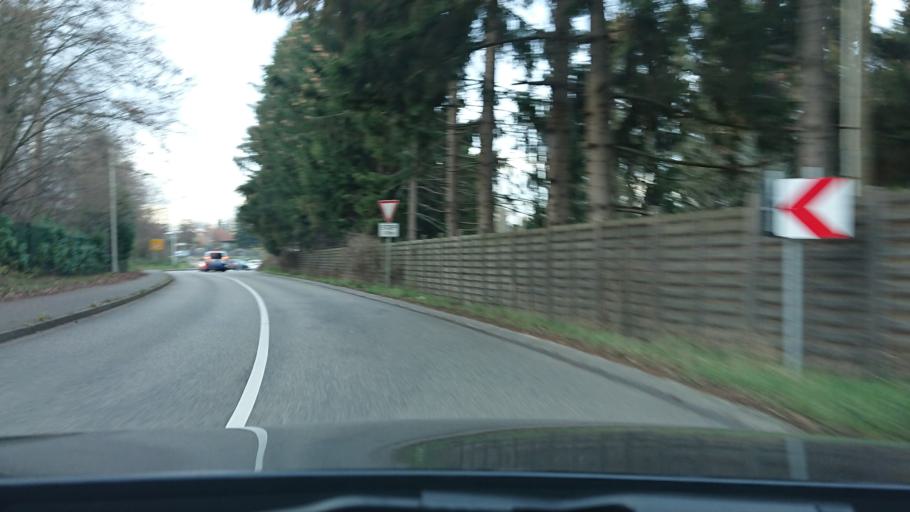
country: DE
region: North Rhine-Westphalia
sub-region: Regierungsbezirk Koln
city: Frechen
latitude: 50.9367
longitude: 6.7873
